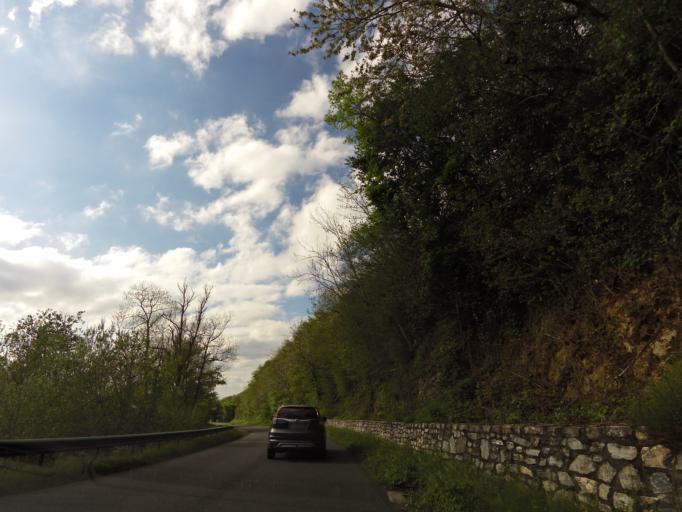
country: FR
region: Midi-Pyrenees
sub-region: Departement du Tarn
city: Soreze
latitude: 43.4286
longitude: 2.0560
